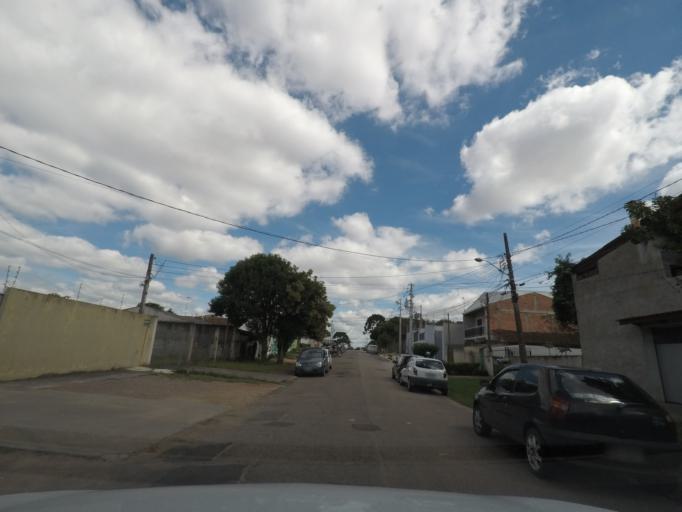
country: BR
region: Parana
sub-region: Sao Jose Dos Pinhais
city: Sao Jose dos Pinhais
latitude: -25.5028
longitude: -49.2198
